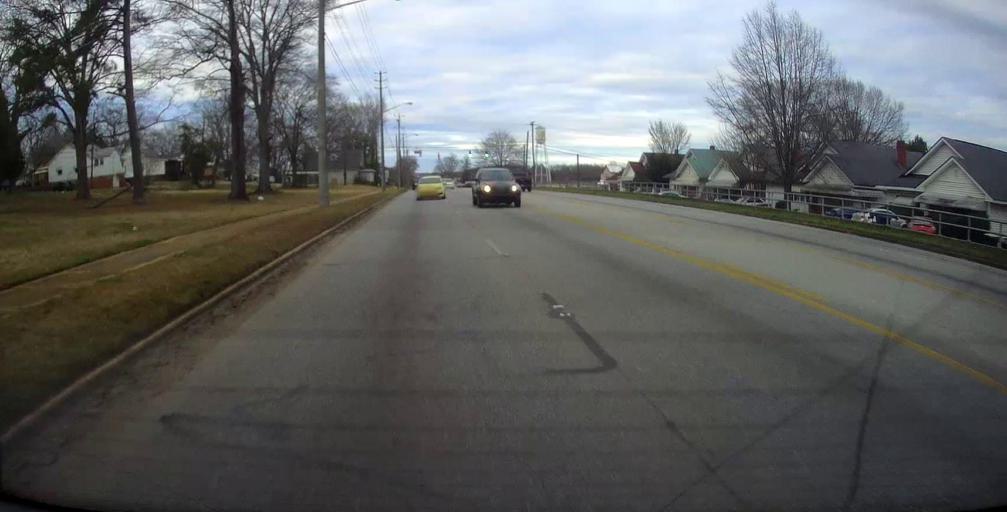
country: US
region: Alabama
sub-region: Chambers County
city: Lanett
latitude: 32.8597
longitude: -85.1906
